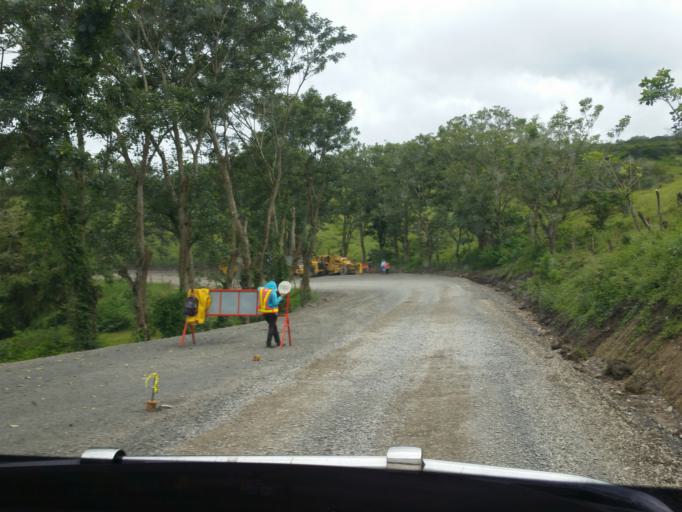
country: NI
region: Jinotega
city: Jinotega
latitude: 13.1752
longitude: -85.9180
